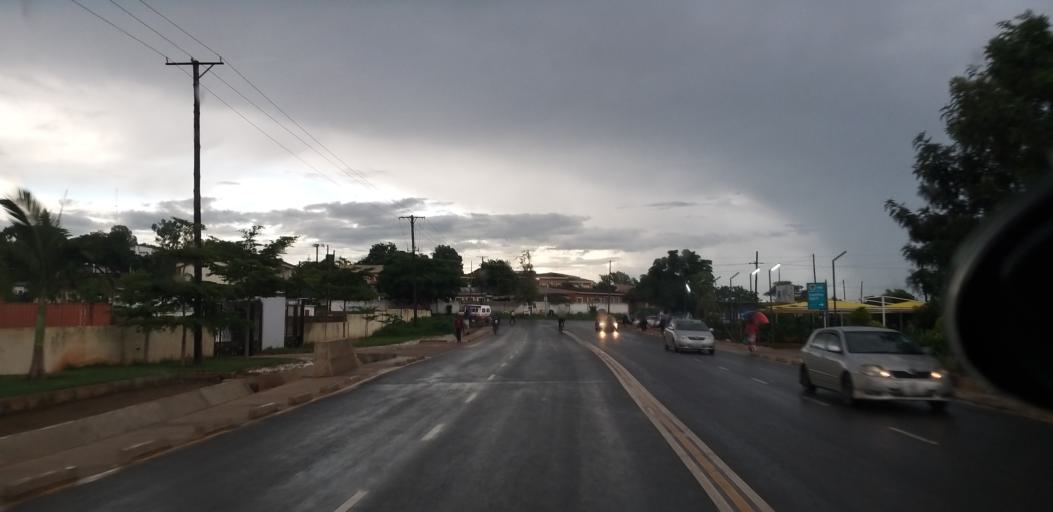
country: ZM
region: Lusaka
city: Lusaka
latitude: -15.4219
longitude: 28.3572
